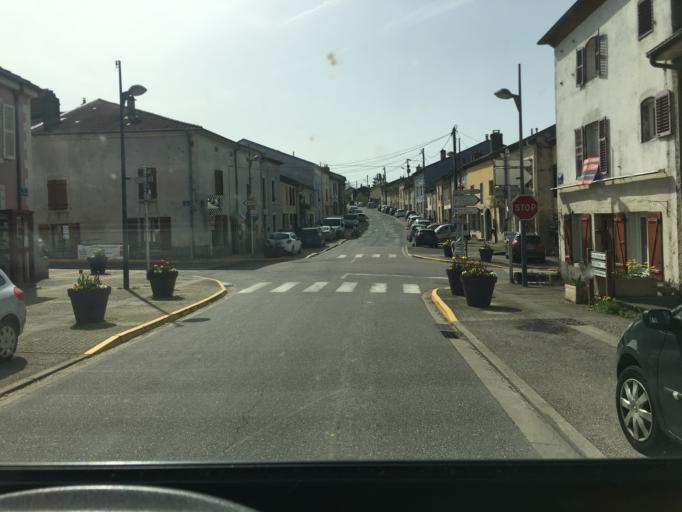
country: FR
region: Lorraine
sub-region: Departement de Meurthe-et-Moselle
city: Chaligny
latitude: 48.6352
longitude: 6.0464
